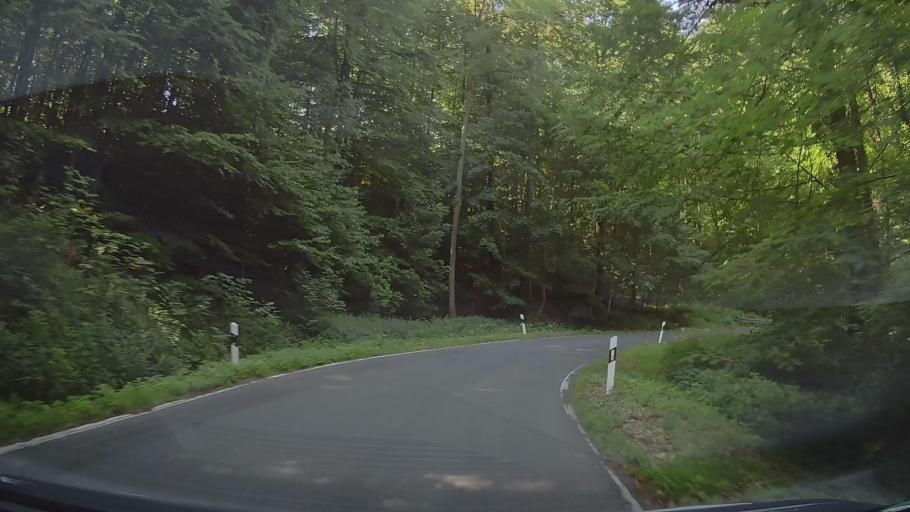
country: DE
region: Lower Saxony
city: Vahlbruch
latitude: 51.9762
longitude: 9.3517
